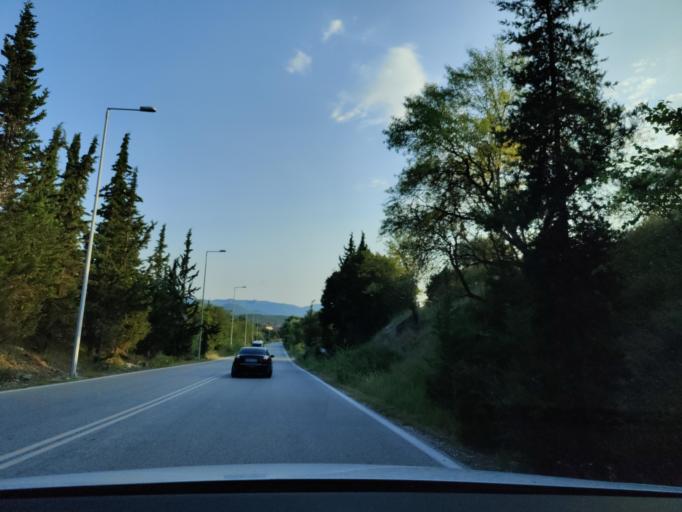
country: GR
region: East Macedonia and Thrace
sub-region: Nomos Kavalas
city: Zygos
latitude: 40.9917
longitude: 24.3781
